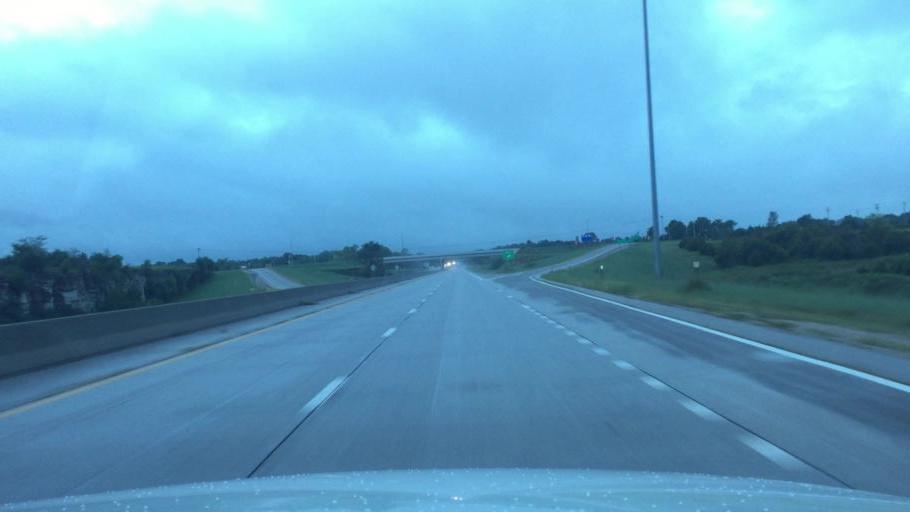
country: US
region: Kansas
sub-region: Neosho County
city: Chanute
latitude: 37.6927
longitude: -95.4796
